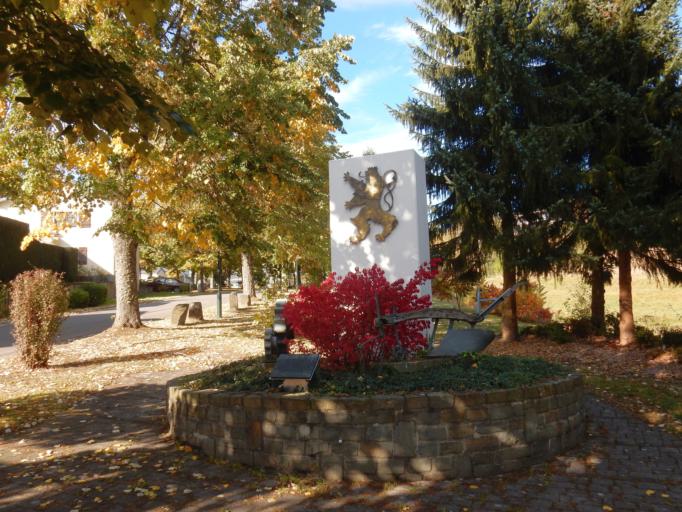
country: LU
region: Diekirch
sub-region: Canton de Wiltz
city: Bavigne
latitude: 49.9079
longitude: 5.8781
